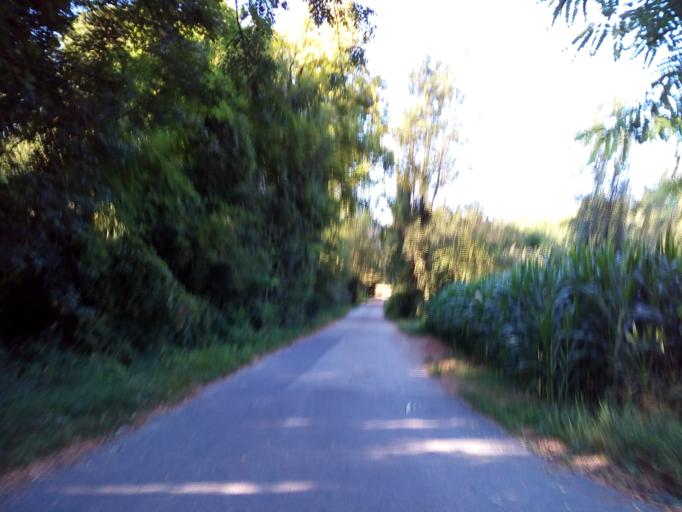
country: FR
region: Rhone-Alpes
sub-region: Departement de l'Isere
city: Goncelin
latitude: 45.3570
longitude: 5.9672
